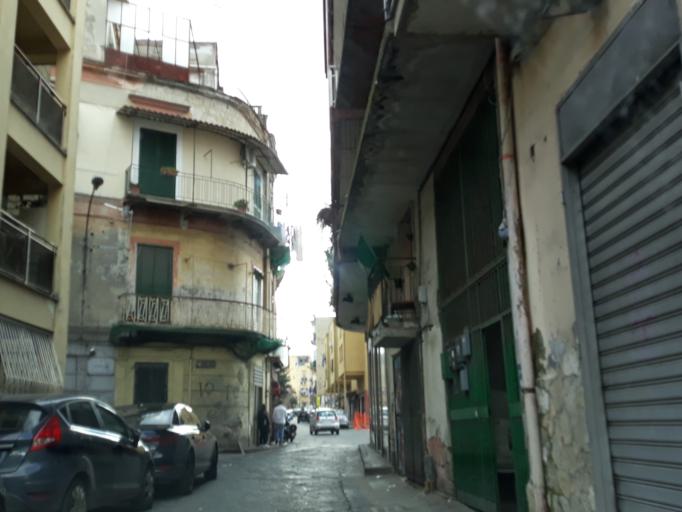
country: IT
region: Campania
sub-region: Provincia di Napoli
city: Mugnano di Napoli
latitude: 40.8901
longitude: 14.2310
